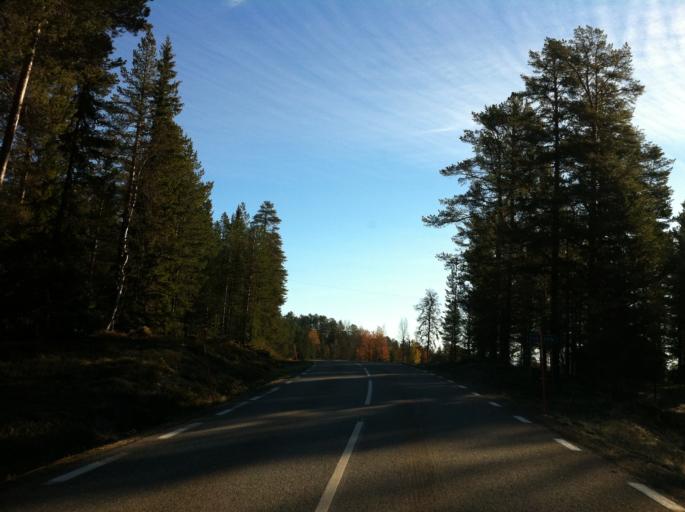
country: NO
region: Hedmark
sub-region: Engerdal
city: Engerdal
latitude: 62.0005
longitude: 12.4491
